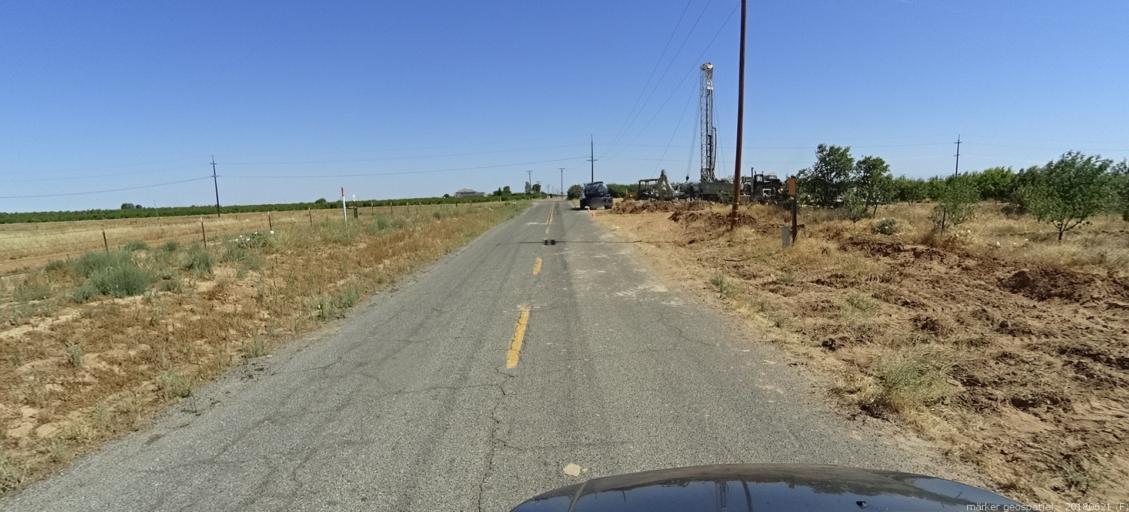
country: US
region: California
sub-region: Madera County
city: Parksdale
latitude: 36.9217
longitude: -119.9396
